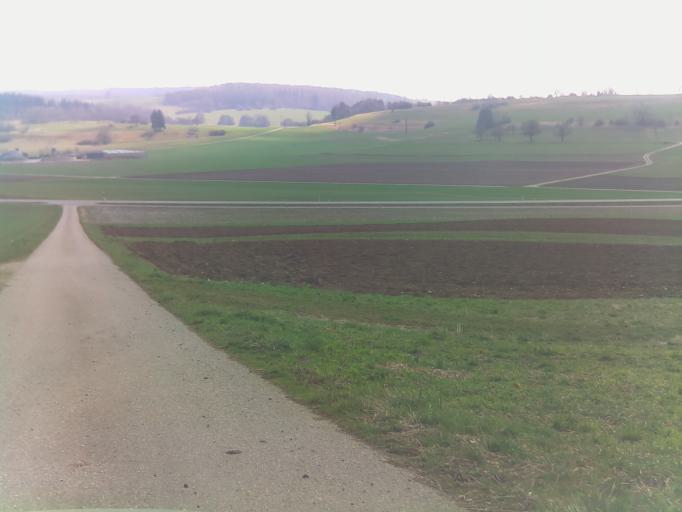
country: DE
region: Baden-Wuerttemberg
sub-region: Tuebingen Region
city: Sankt Johann
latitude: 48.4484
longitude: 9.3743
